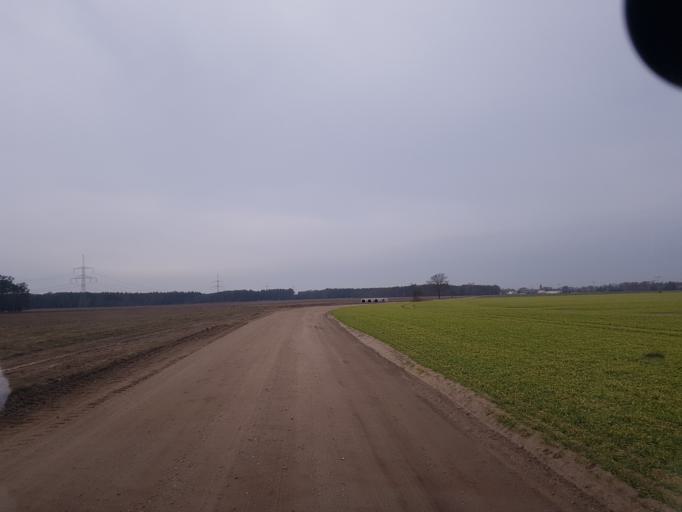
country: DE
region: Brandenburg
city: Sonnewalde
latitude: 51.6621
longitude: 13.6649
